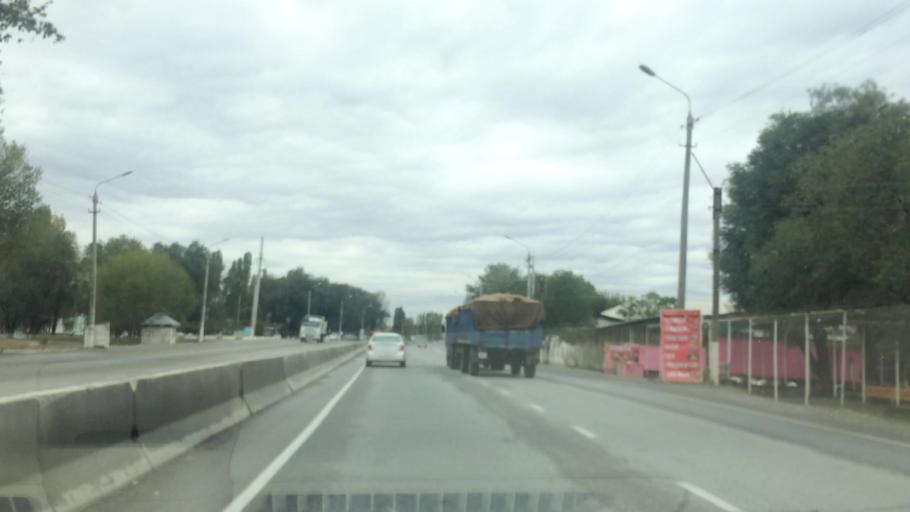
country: UZ
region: Jizzax
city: Jizzax
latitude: 39.9860
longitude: 67.5759
